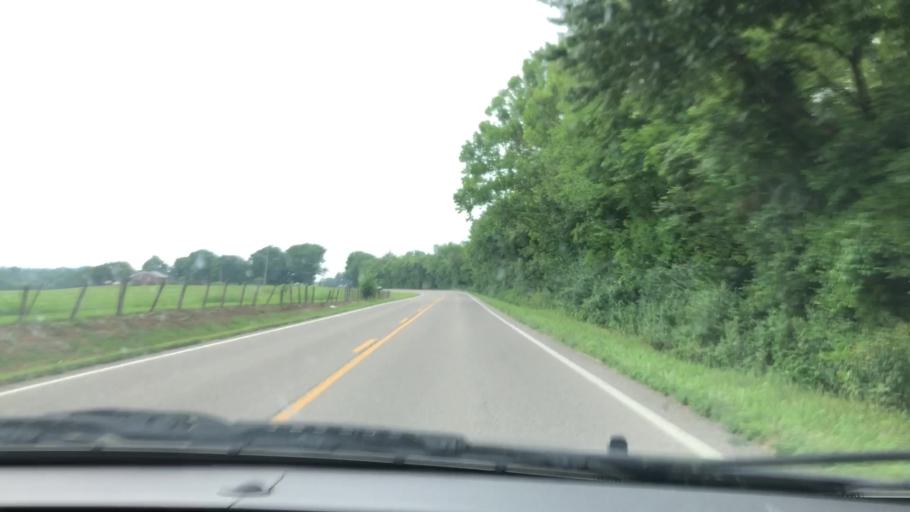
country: US
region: Tennessee
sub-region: Maury County
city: Spring Hill
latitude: 35.7616
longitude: -87.0072
